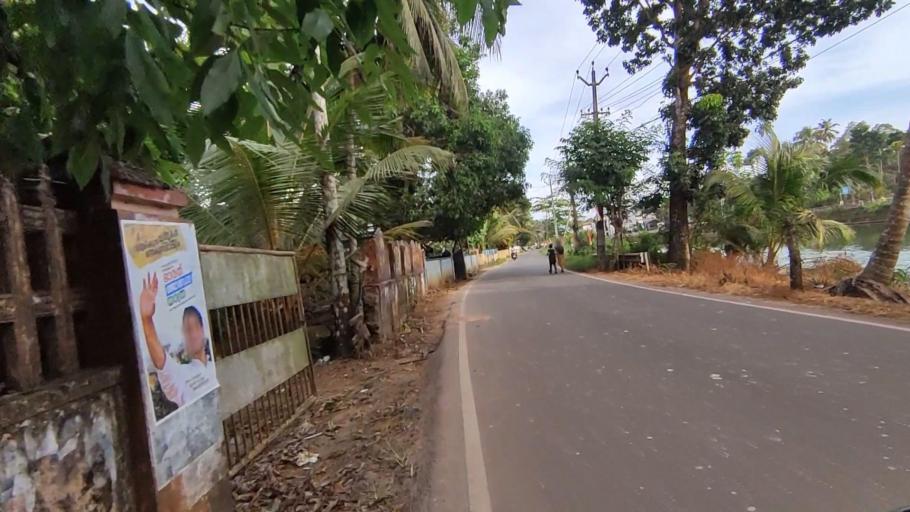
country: IN
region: Kerala
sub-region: Kottayam
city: Kottayam
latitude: 9.5923
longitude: 76.4961
